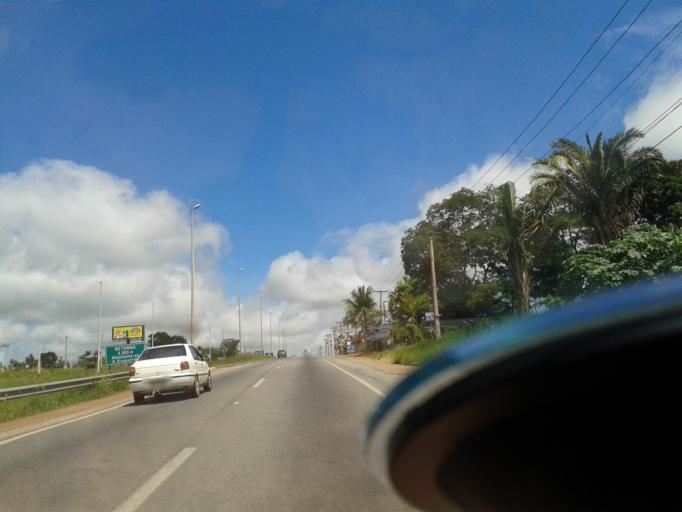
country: BR
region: Goias
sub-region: Goiania
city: Goiania
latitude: -16.6298
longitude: -49.3498
